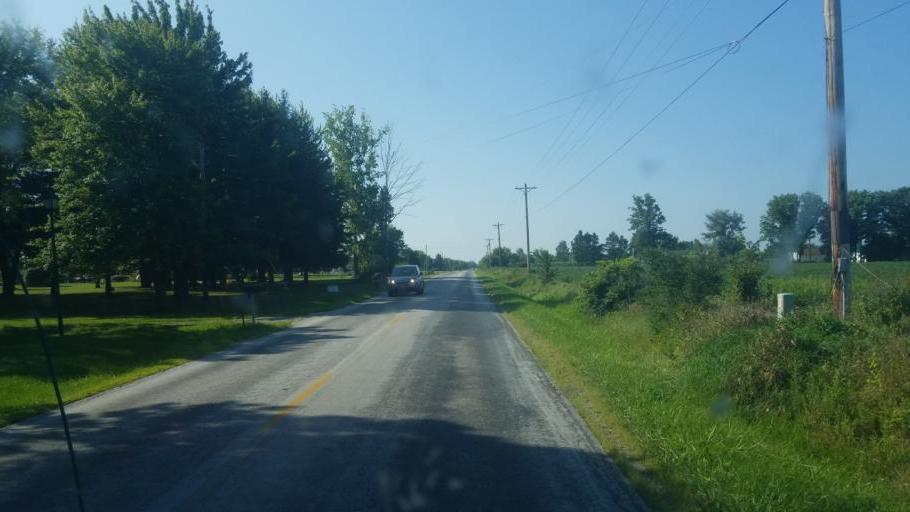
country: US
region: Ohio
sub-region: Lorain County
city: Wellington
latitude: 41.0948
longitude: -82.1613
